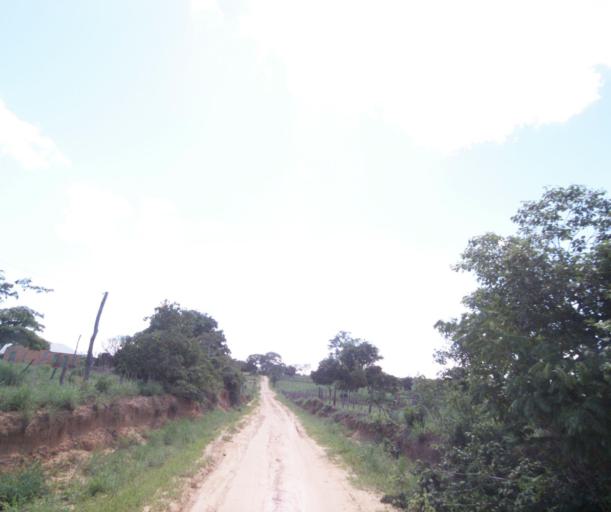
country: BR
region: Bahia
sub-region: Carinhanha
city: Carinhanha
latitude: -14.2345
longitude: -44.3133
